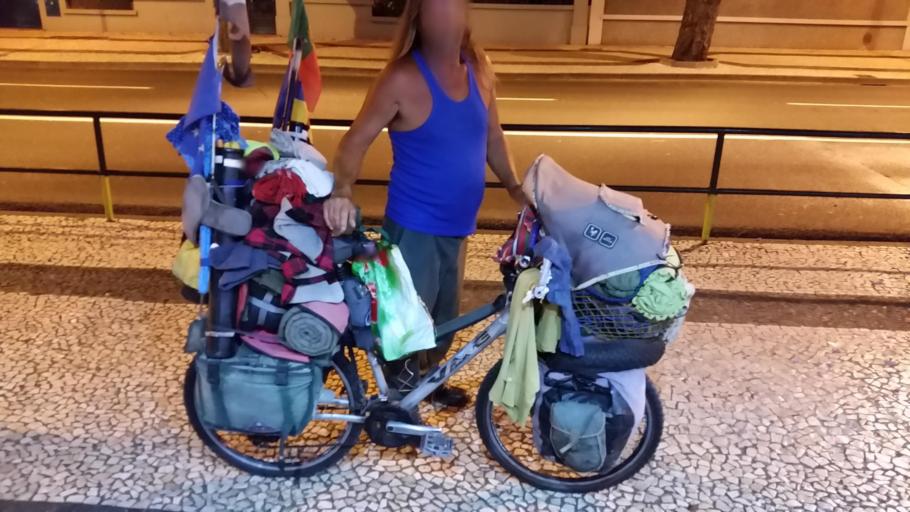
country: PT
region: Madeira
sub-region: Funchal
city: Funchal
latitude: 32.6444
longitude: -16.9189
